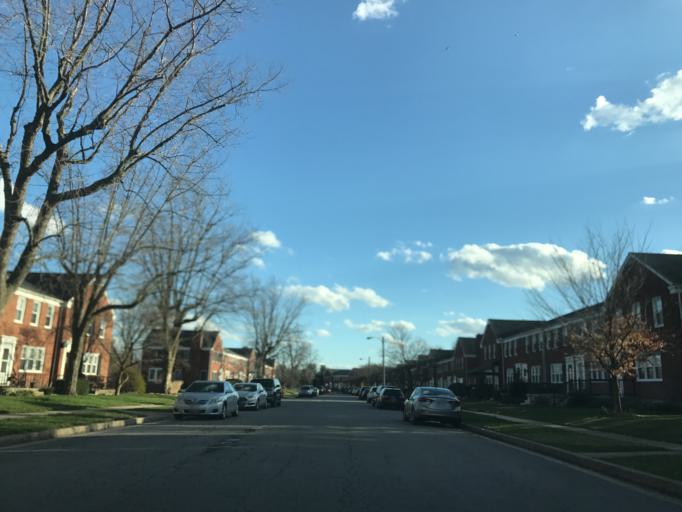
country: US
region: Maryland
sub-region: Baltimore County
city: Towson
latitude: 39.3948
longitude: -76.5742
